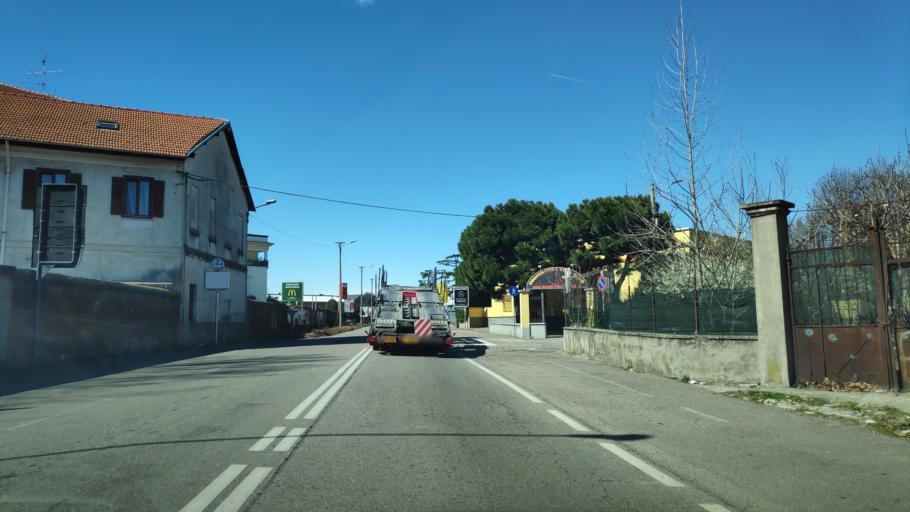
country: IT
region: Lombardy
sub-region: Provincia di Varese
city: Castellanza
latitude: 45.6155
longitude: 8.8831
